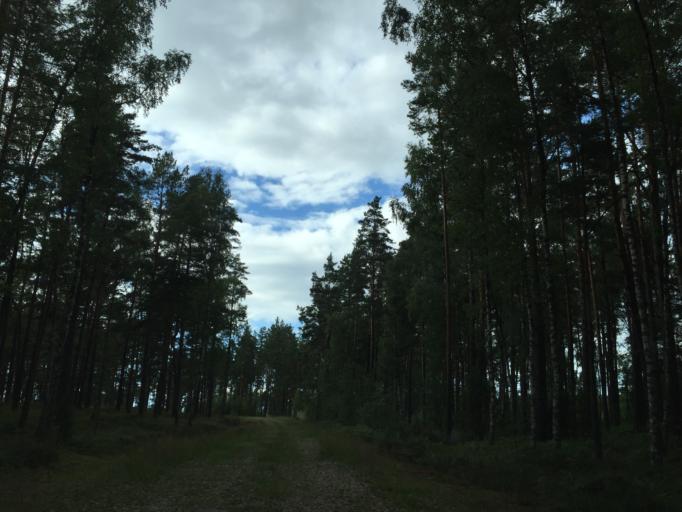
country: LV
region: Saulkrastu
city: Saulkrasti
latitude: 57.1757
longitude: 24.3742
